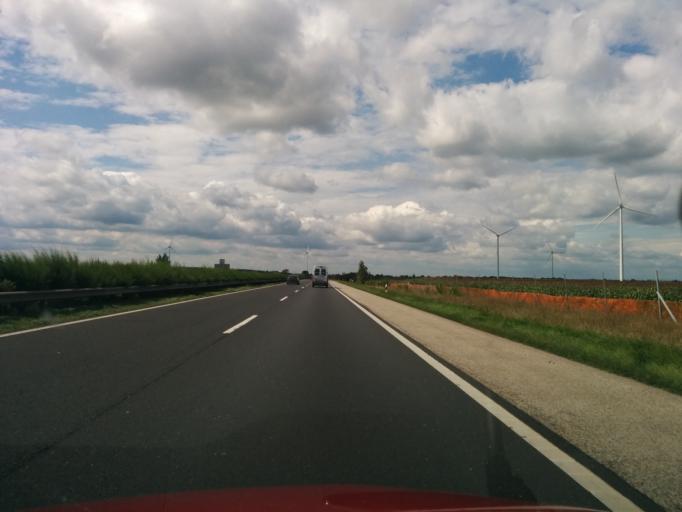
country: HU
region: Komarom-Esztergom
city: Babolna
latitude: 47.6803
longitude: 17.9648
